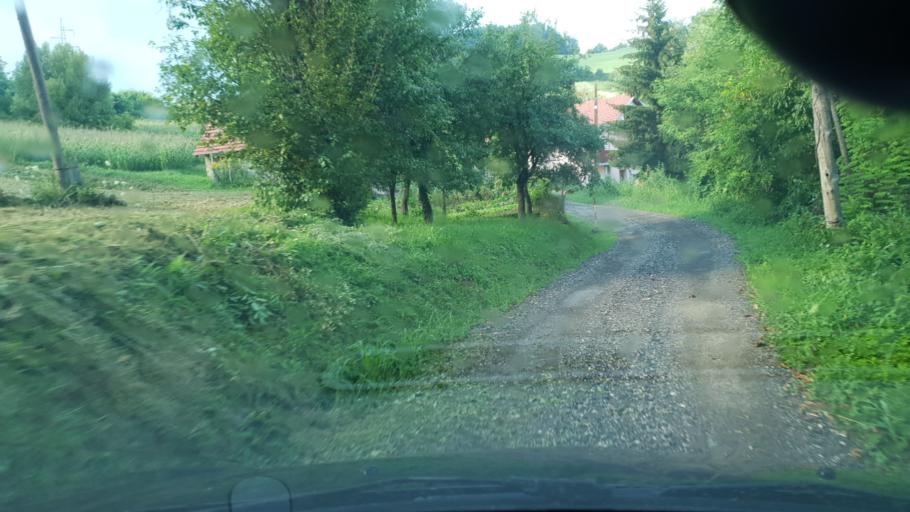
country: HR
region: Krapinsko-Zagorska
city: Mihovljan
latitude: 46.0972
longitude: 15.9190
